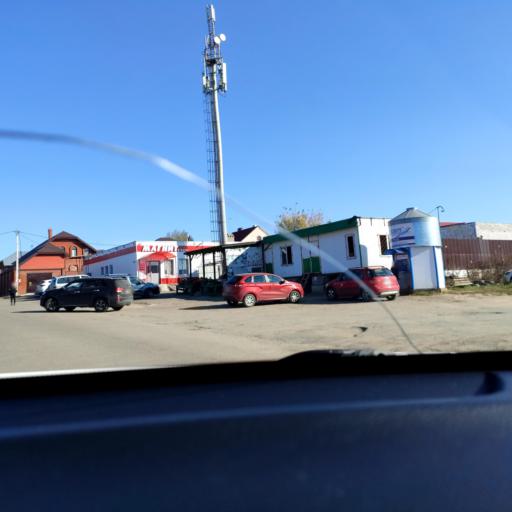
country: RU
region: Tatarstan
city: Vysokaya Gora
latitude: 55.8495
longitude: 49.2241
